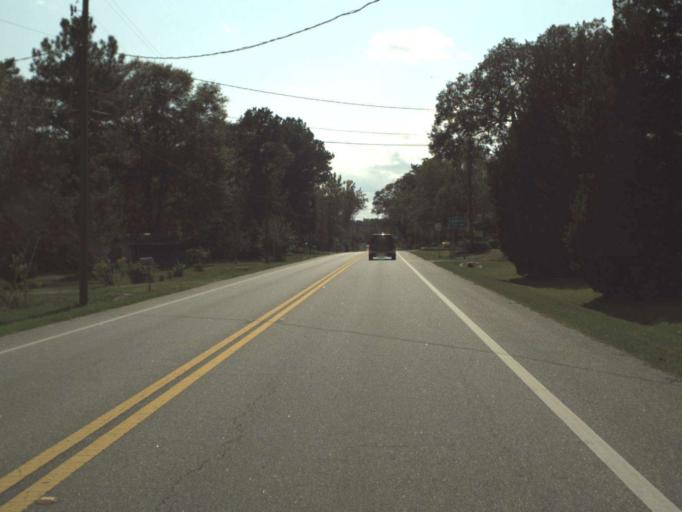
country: US
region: Florida
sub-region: Holmes County
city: Bonifay
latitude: 30.8081
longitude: -85.6762
